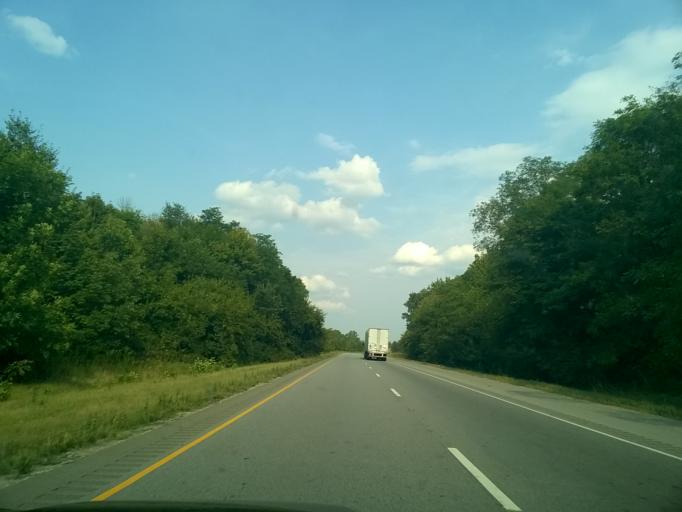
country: US
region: Indiana
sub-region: Vigo County
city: Seelyville
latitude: 39.4454
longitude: -87.2534
